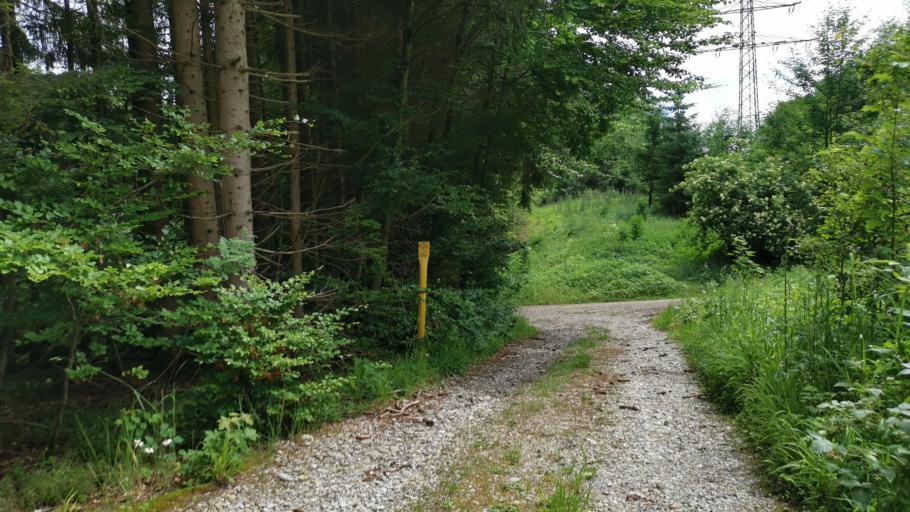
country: DE
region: Bavaria
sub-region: Upper Bavaria
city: Schaftlarn
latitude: 48.0071
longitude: 11.4600
